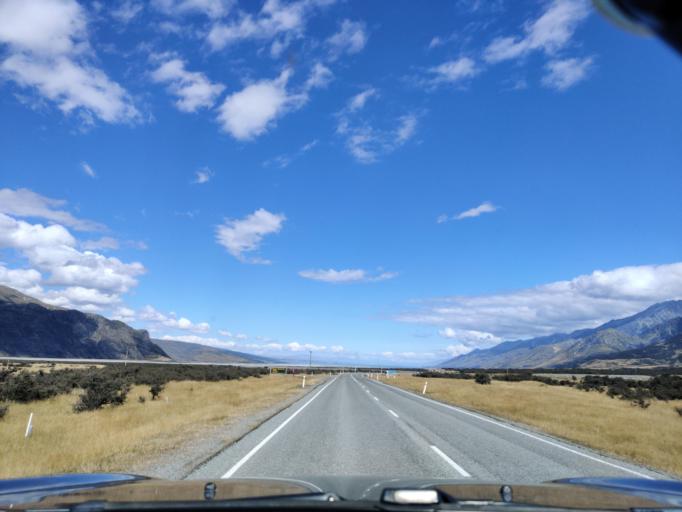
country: NZ
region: Canterbury
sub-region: Timaru District
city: Pleasant Point
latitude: -43.7650
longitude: 170.1228
